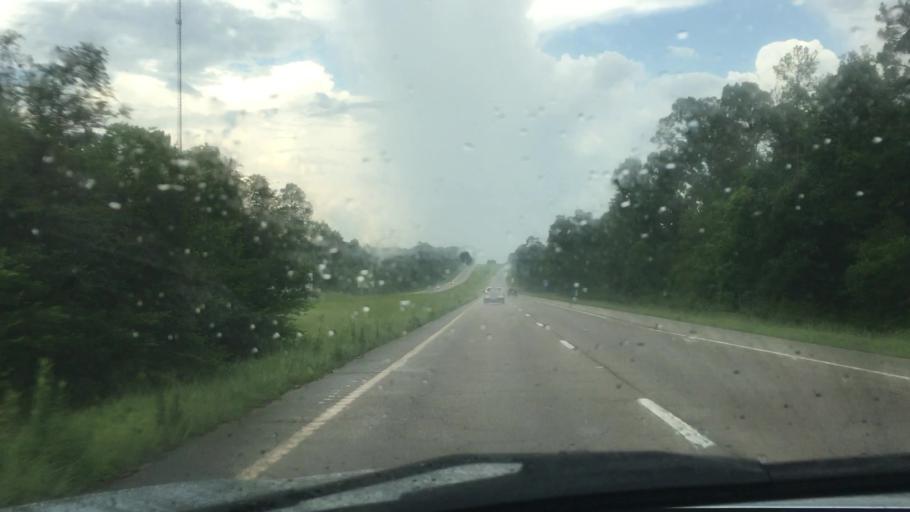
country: US
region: Mississippi
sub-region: Lamar County
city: Purvis
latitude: 31.1446
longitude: -89.3659
